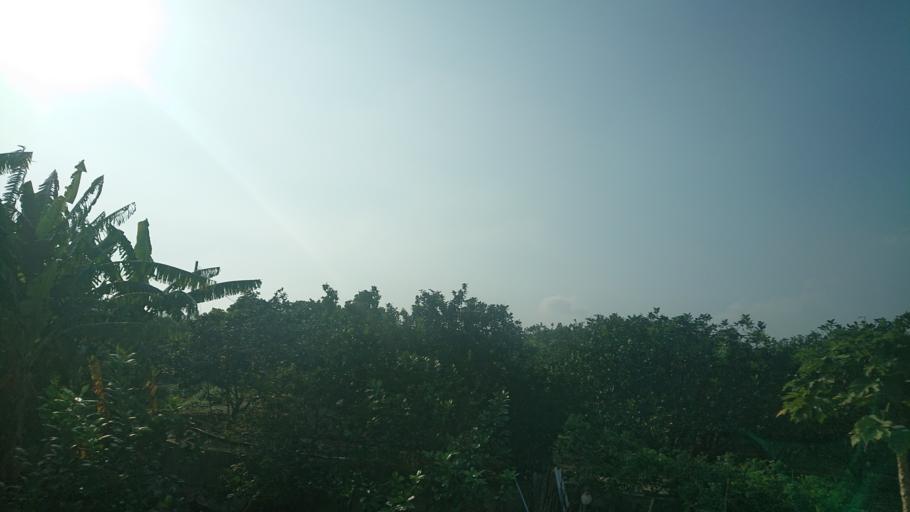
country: TW
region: Taiwan
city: Xinying
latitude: 23.1613
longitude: 120.2502
